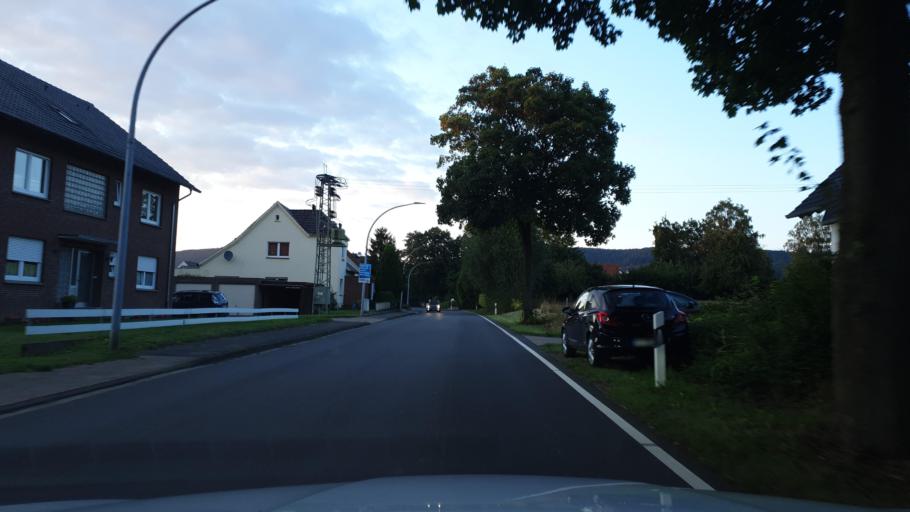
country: DE
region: North Rhine-Westphalia
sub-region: Regierungsbezirk Detmold
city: Huellhorst
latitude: 52.2704
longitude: 8.7137
